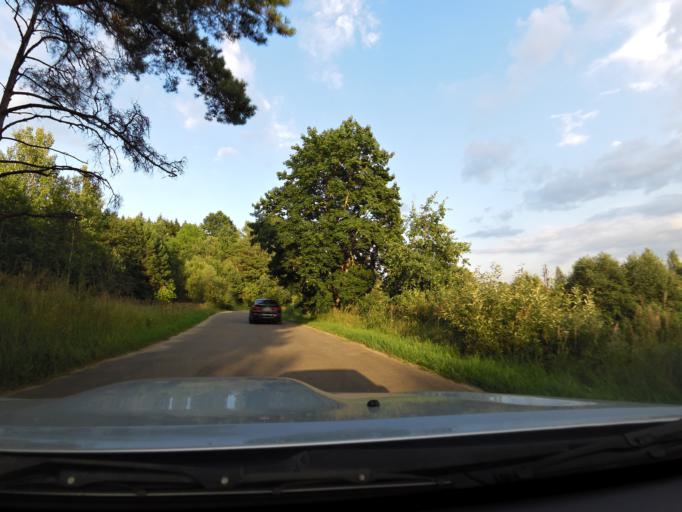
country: LT
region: Siauliu apskritis
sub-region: Siauliai
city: Siauliai
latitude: 55.8550
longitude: 23.1289
